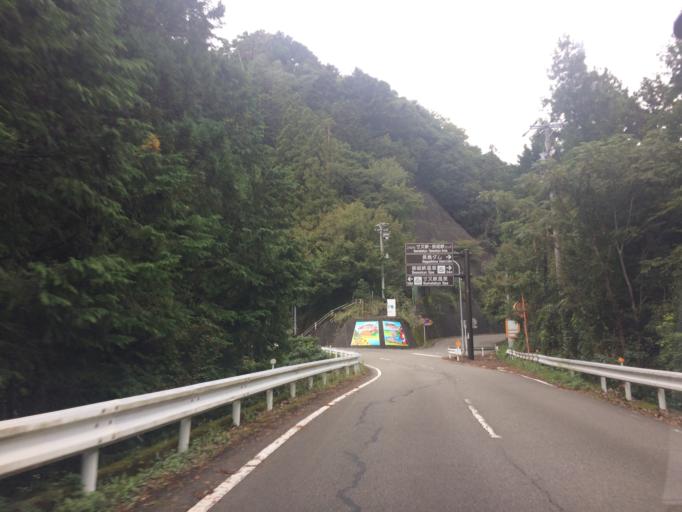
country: JP
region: Shizuoka
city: Shizuoka-shi
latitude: 35.1538
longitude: 138.1444
